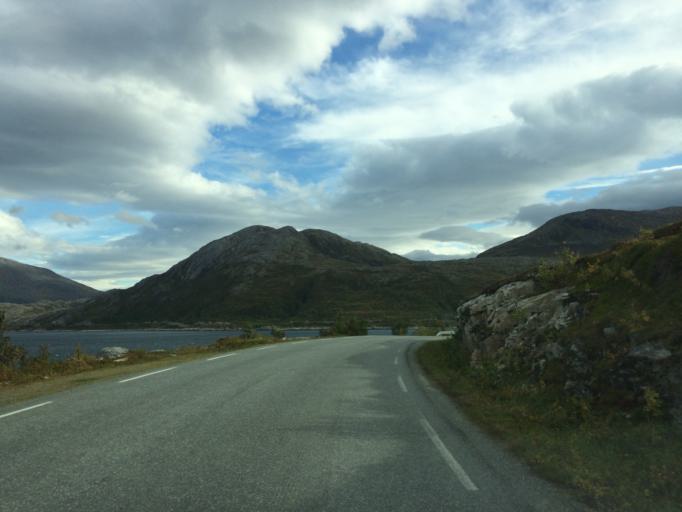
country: NO
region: Troms
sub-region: Lenvik
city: Finnsnes
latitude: 69.6214
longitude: 18.0742
